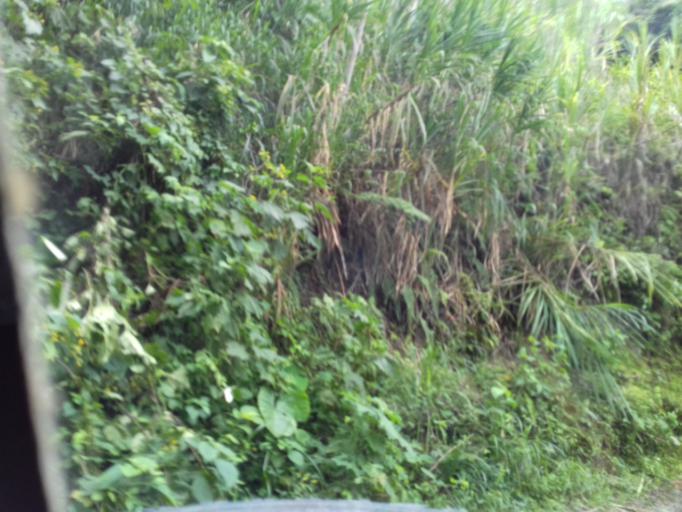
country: CO
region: Tolima
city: Libano
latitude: 4.9250
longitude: -75.0952
